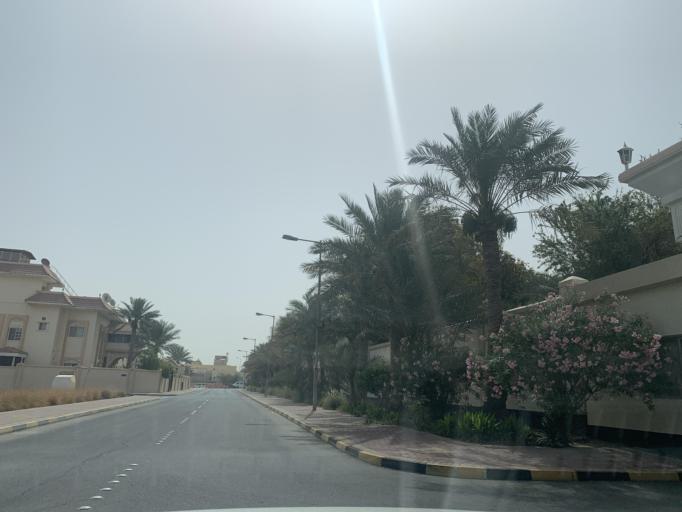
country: BH
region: Northern
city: Madinat `Isa
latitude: 26.1544
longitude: 50.5166
